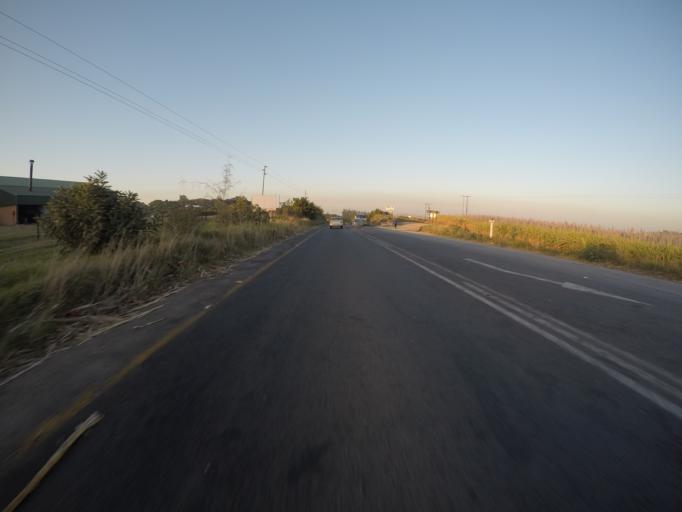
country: ZA
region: KwaZulu-Natal
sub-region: uThungulu District Municipality
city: Empangeni
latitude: -28.8093
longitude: 31.8916
